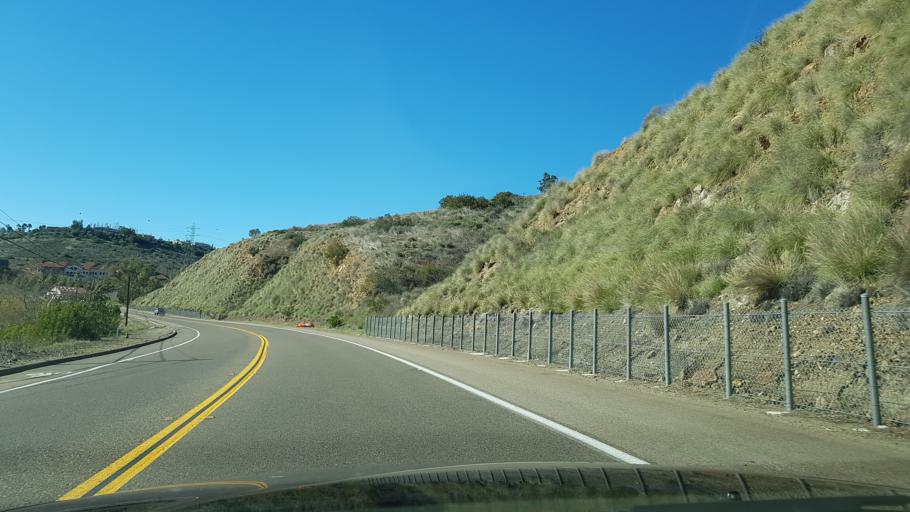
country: US
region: California
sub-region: San Diego County
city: Rancho Santa Fe
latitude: 33.0432
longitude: -117.1522
